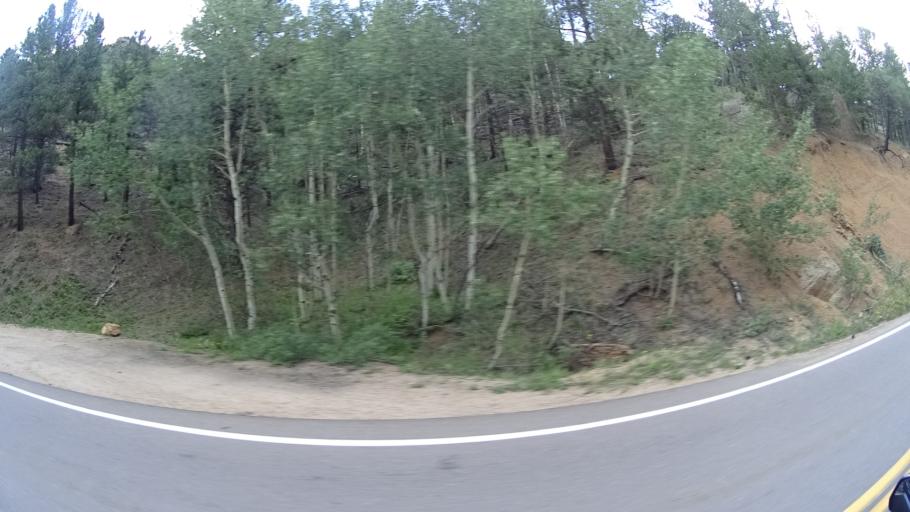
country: US
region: Colorado
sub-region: El Paso County
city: Cascade-Chipita Park
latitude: 38.9073
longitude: -105.0128
